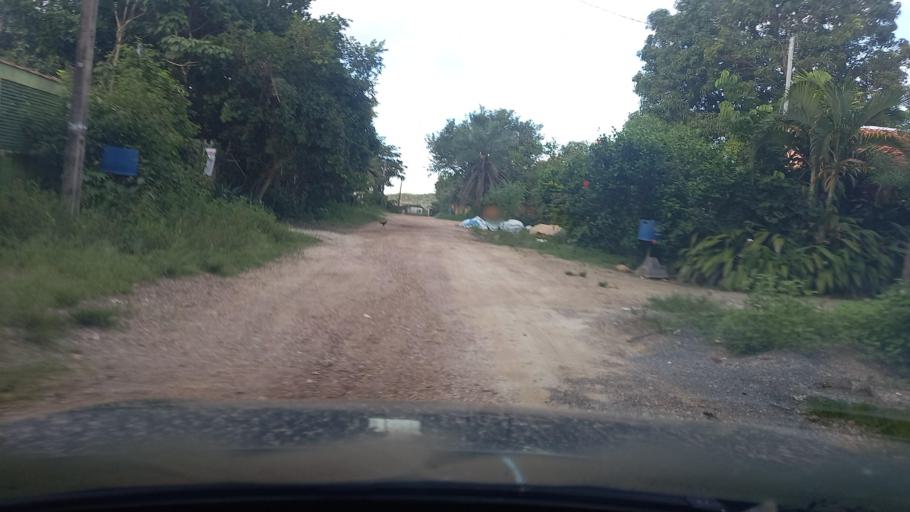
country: BR
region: Goias
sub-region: Cavalcante
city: Cavalcante
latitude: -13.7922
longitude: -47.4639
